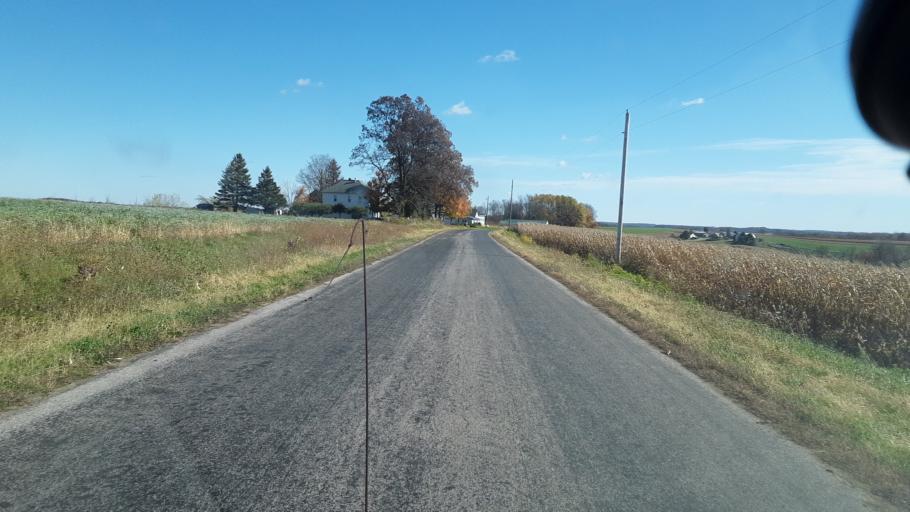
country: US
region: Wisconsin
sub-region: Vernon County
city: Hillsboro
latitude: 43.6925
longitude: -90.4322
